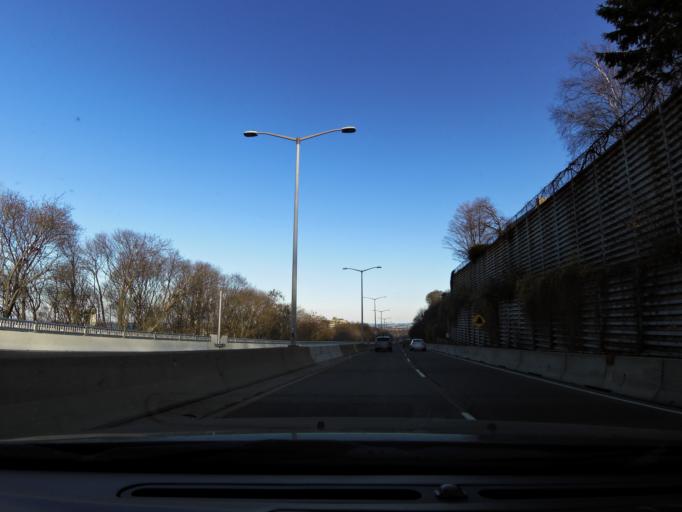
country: CA
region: Ontario
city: Hamilton
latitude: 43.2451
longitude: -79.8740
